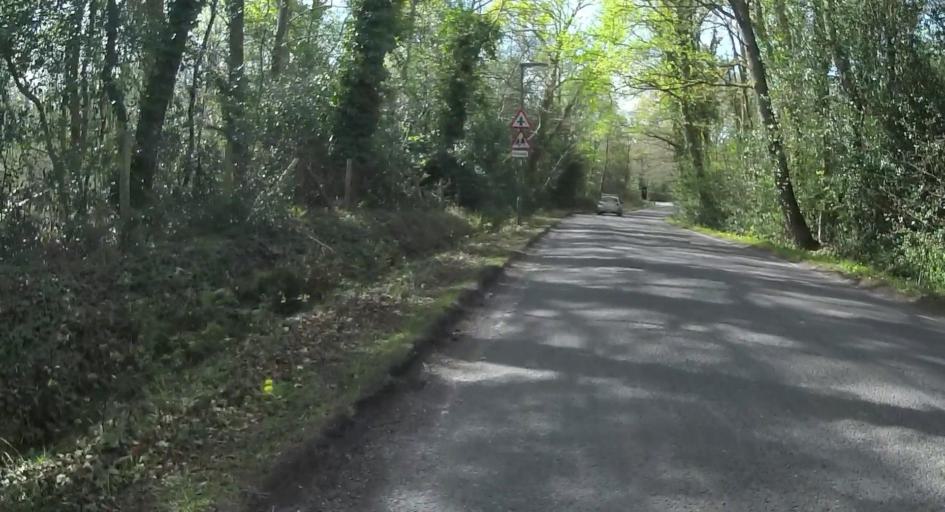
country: GB
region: England
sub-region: Surrey
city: Farnham
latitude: 51.1797
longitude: -0.8094
